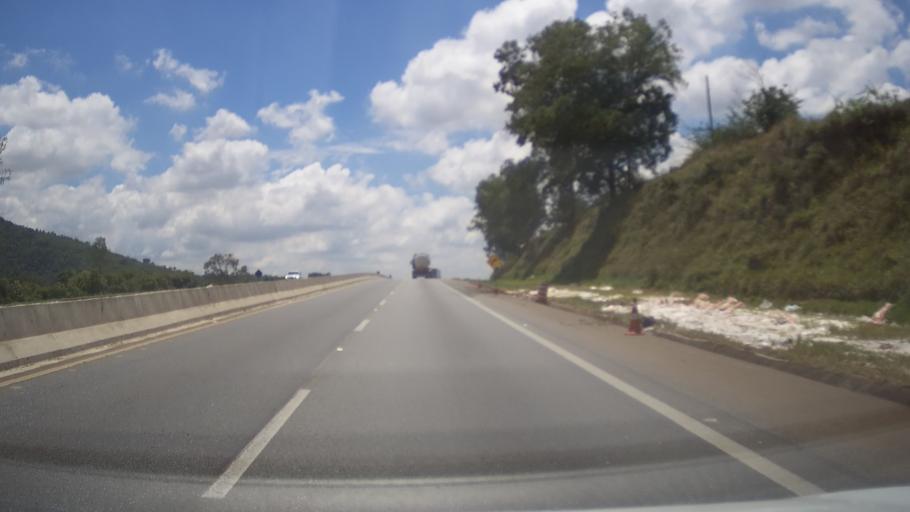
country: BR
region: Minas Gerais
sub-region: Campanha
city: Campanha
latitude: -21.8034
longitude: -45.4730
